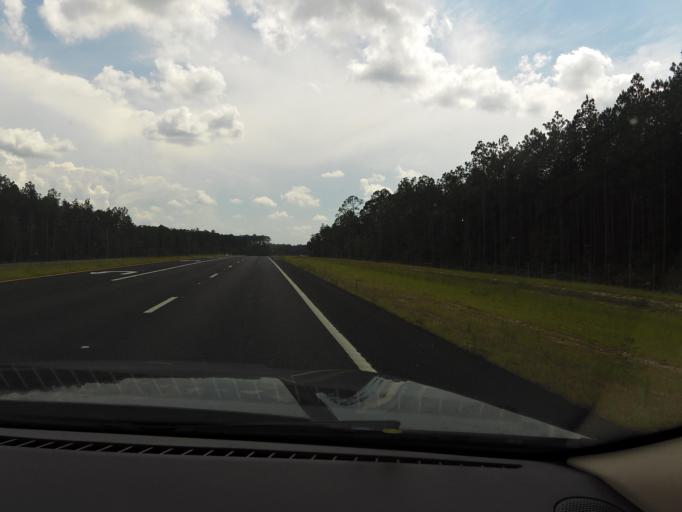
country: US
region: Florida
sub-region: Duval County
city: Baldwin
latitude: 30.3164
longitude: -81.9768
